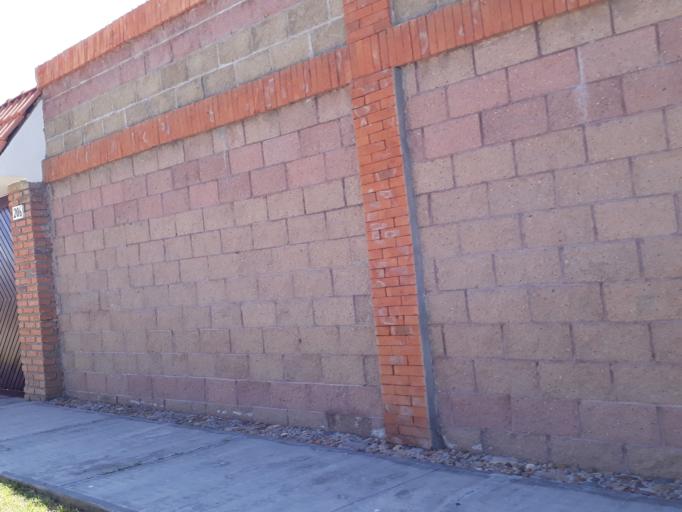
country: MX
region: Aguascalientes
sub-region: Aguascalientes
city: San Sebastian [Fraccionamiento]
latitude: 21.7905
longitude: -102.2754
